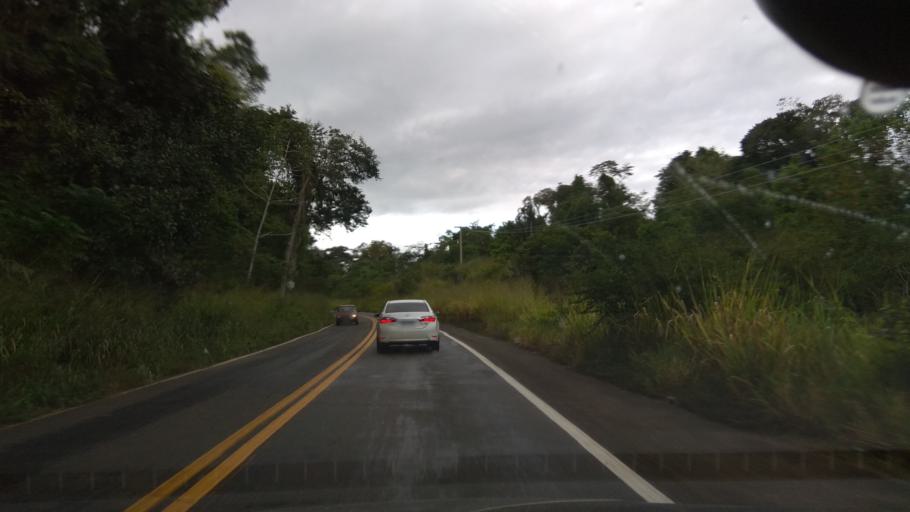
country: BR
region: Bahia
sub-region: Ubata
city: Ubata
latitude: -14.2305
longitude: -39.4544
